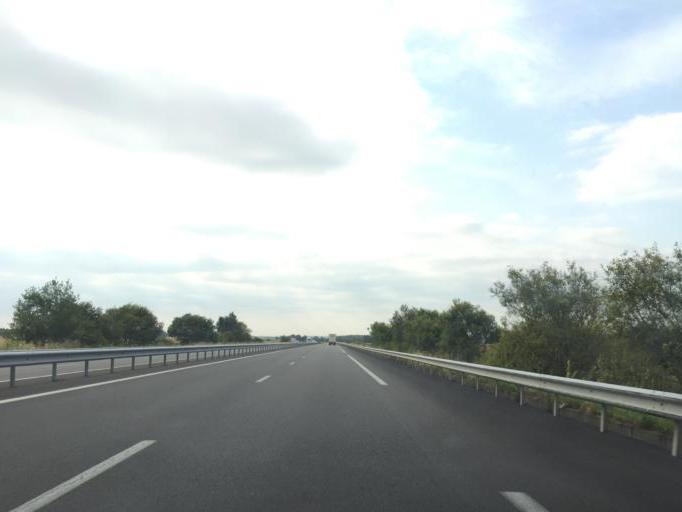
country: FR
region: Auvergne
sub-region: Departement de l'Allier
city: Saint-Francois
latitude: 46.4627
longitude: 3.8878
